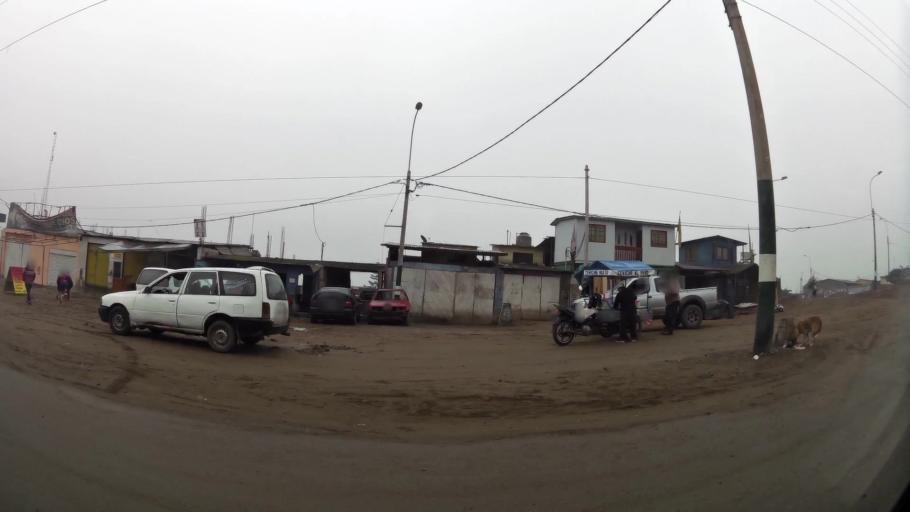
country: PE
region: Lima
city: Ventanilla
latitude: -11.8375
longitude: -77.1395
